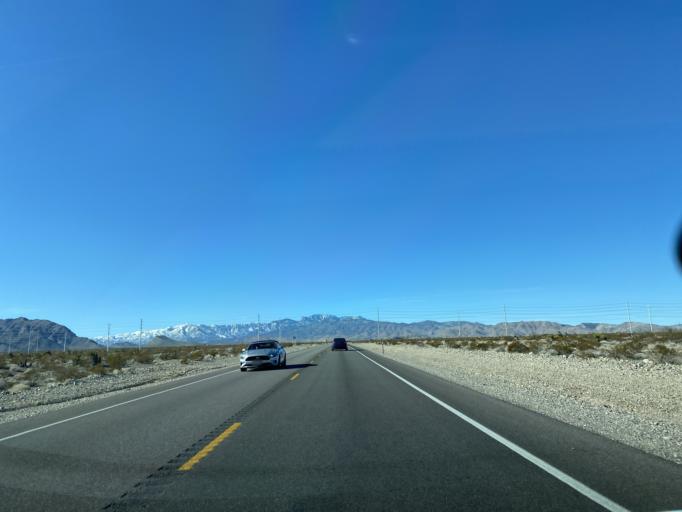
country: US
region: Nevada
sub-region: Clark County
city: Summerlin South
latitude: 36.3262
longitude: -115.3219
